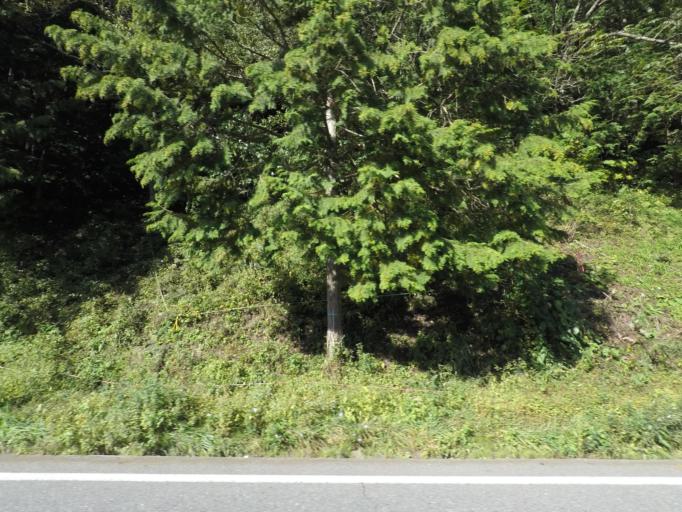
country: JP
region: Nagano
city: Ina
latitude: 35.9612
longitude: 137.7662
